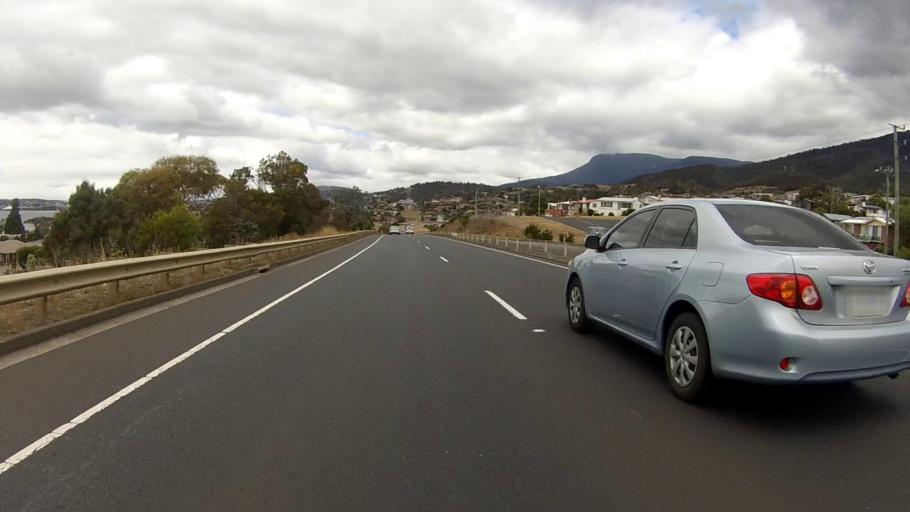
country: AU
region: Tasmania
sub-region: Glenorchy
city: Berriedale
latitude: -42.8075
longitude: 147.2494
